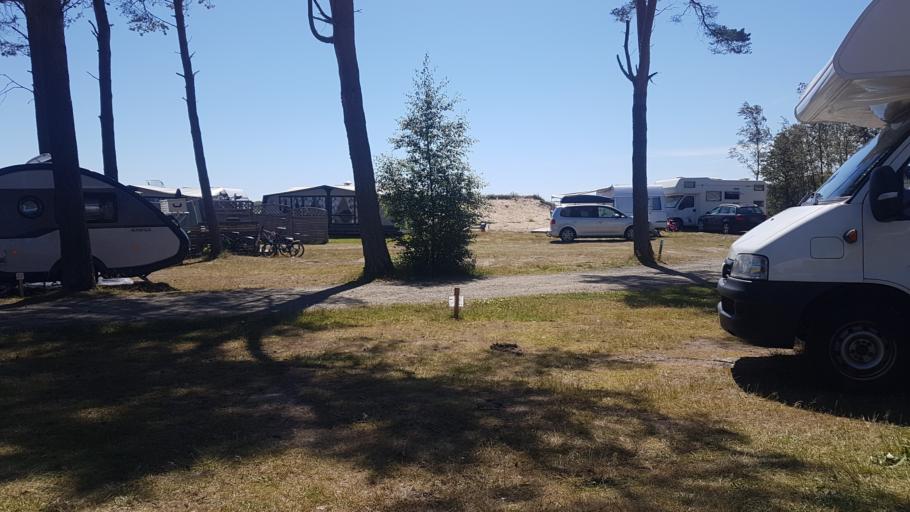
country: NO
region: Vest-Agder
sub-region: Farsund
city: Farsund
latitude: 58.0671
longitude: 6.7965
